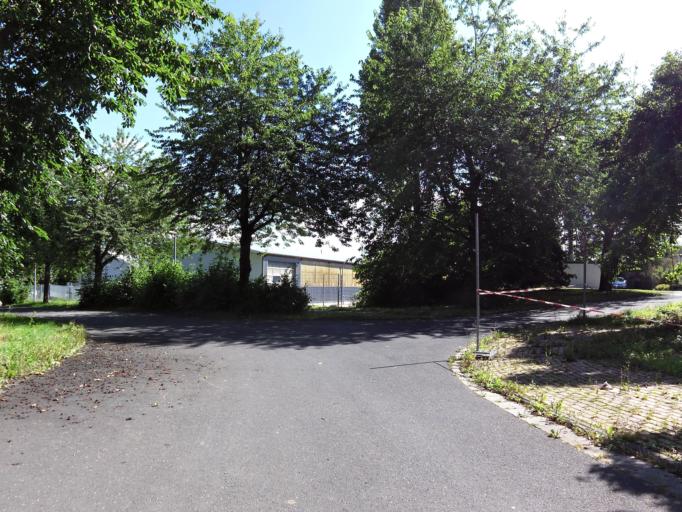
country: DE
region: Thuringia
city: Krauthausen
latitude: 51.0092
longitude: 10.2551
